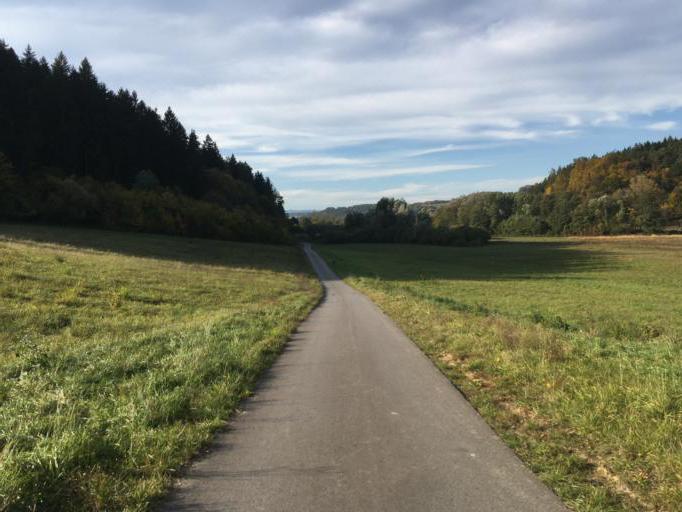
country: SK
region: Trenciansky
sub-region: Okres Povazska Bystrica
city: Povazska Bystrica
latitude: 49.0574
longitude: 18.3944
